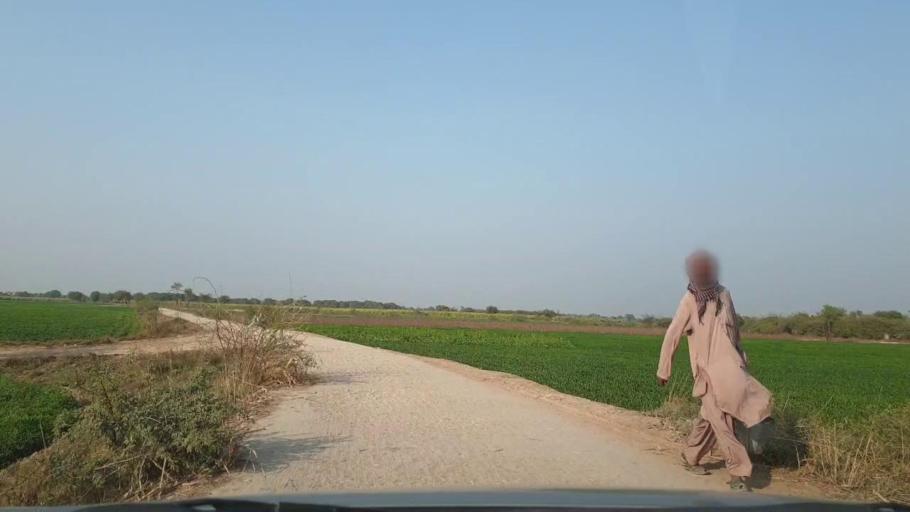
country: PK
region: Sindh
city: Tando Adam
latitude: 25.6719
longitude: 68.6372
